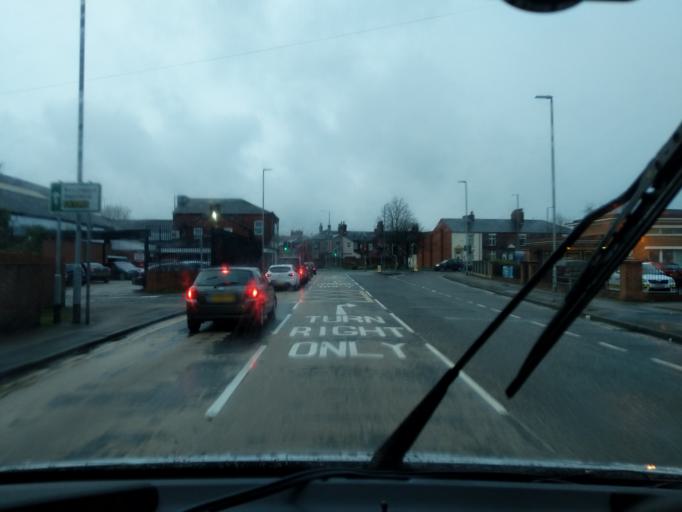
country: GB
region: England
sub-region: St. Helens
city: St Helens
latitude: 53.4554
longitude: -2.7467
